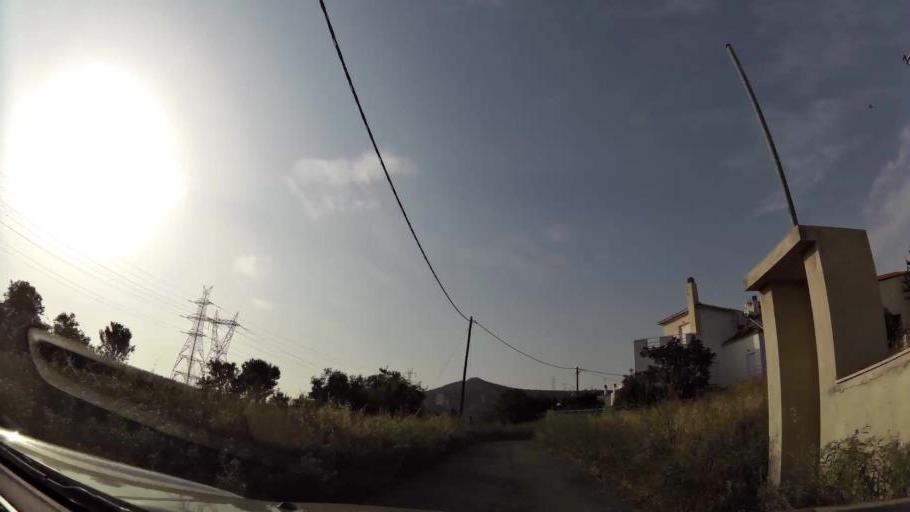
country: GR
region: Central Macedonia
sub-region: Nomos Thessalonikis
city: Oraiokastro
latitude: 40.7203
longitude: 22.9017
